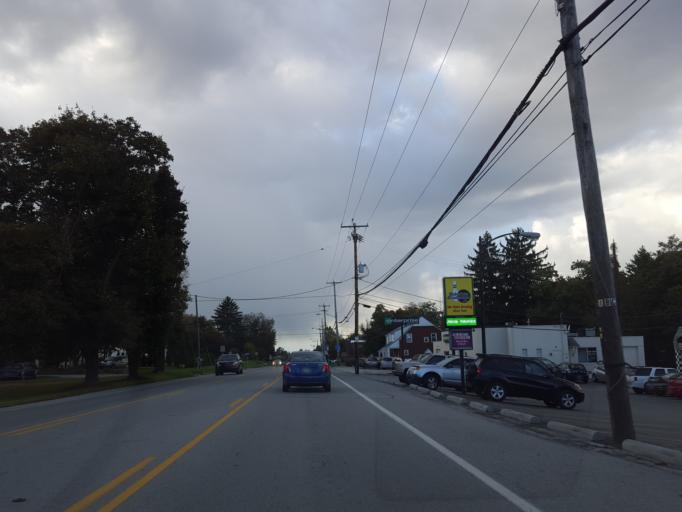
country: US
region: Pennsylvania
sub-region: York County
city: Valley View
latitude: 39.9404
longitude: -76.6990
